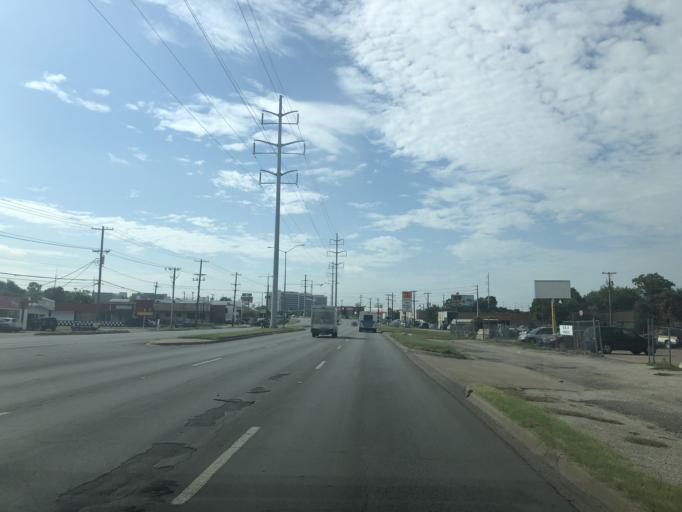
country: US
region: Texas
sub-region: Dallas County
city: University Park
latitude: 32.8292
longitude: -96.8576
